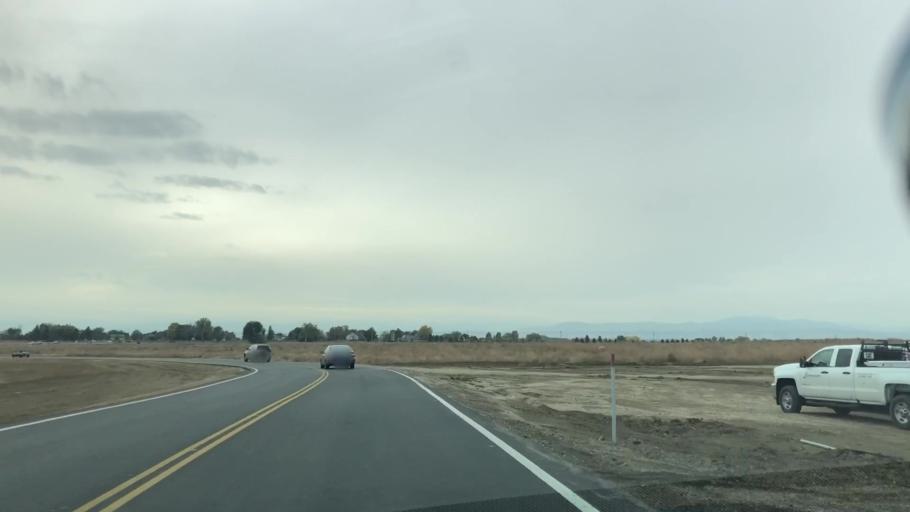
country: US
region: Colorado
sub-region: Larimer County
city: Loveland
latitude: 40.4304
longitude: -105.0124
